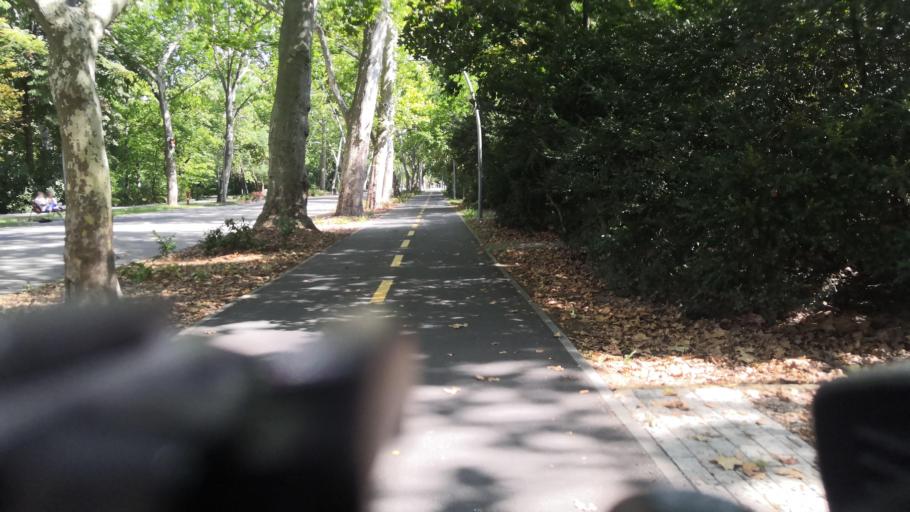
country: HU
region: Csongrad
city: Szeged
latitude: 46.2479
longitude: 20.1625
